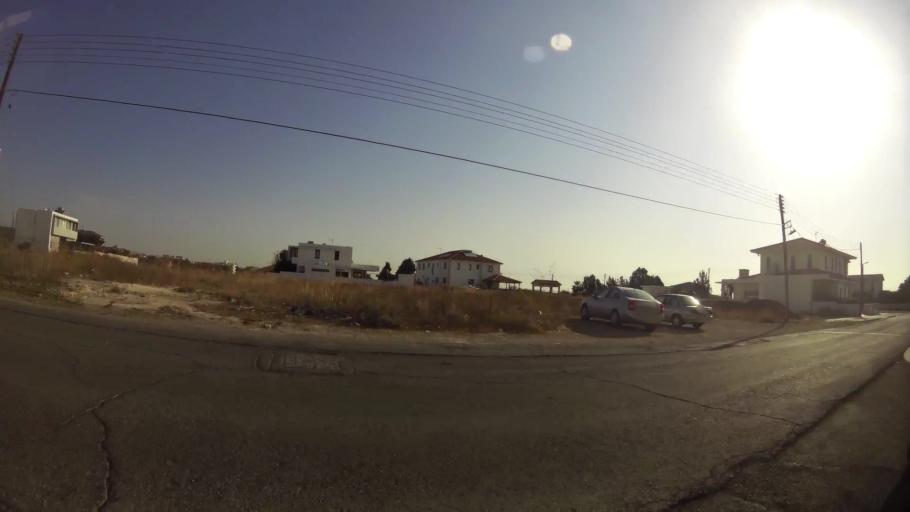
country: CY
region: Larnaka
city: Aradippou
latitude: 34.9370
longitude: 33.5978
